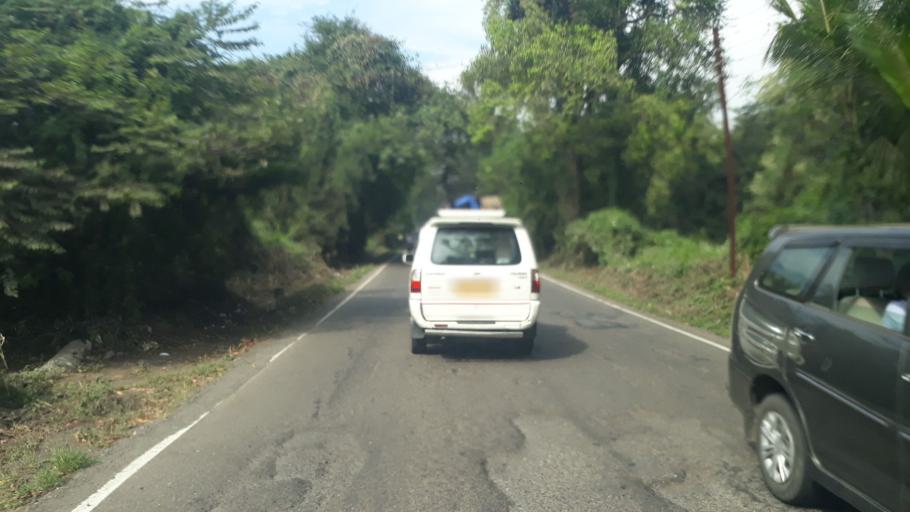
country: IN
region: Maharashtra
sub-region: Raigarh
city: Alibag
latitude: 18.6916
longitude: 72.9695
